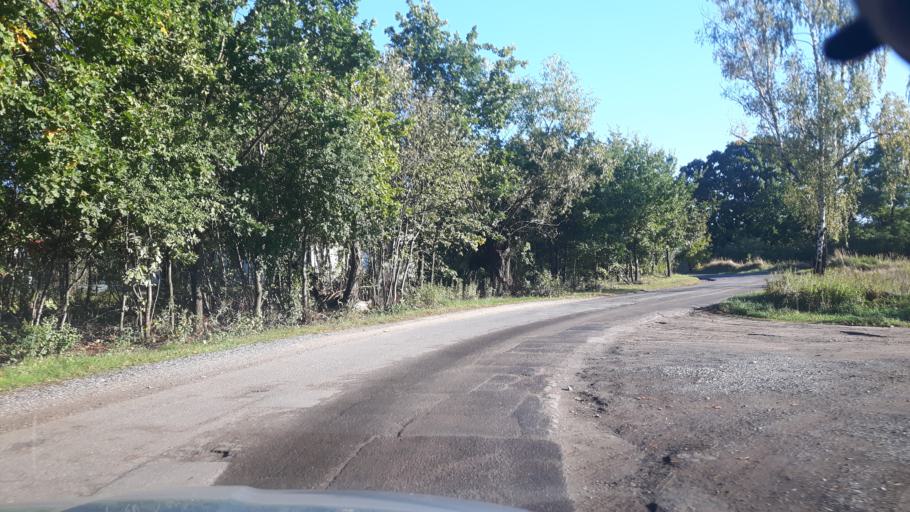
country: PL
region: Masovian Voivodeship
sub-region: Warszawa
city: Bialoleka
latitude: 52.3337
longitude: 20.9987
